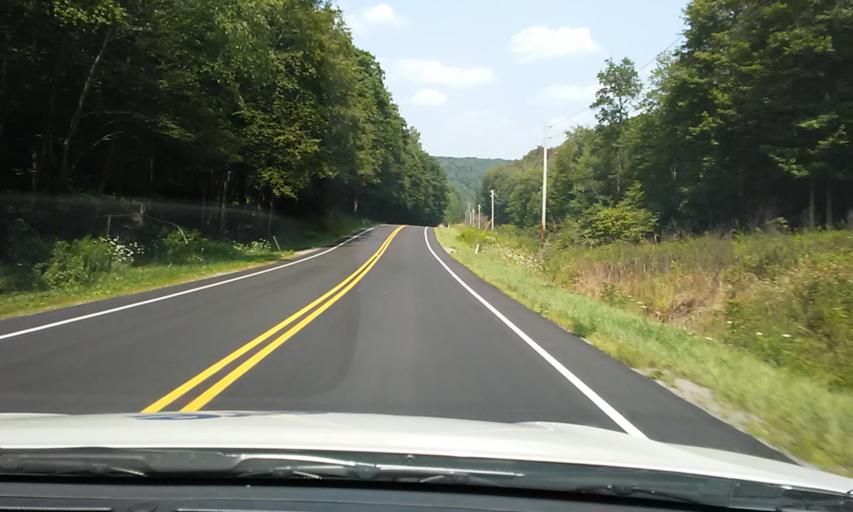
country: US
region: Pennsylvania
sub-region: Elk County
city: Saint Marys
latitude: 41.4588
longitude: -78.4296
